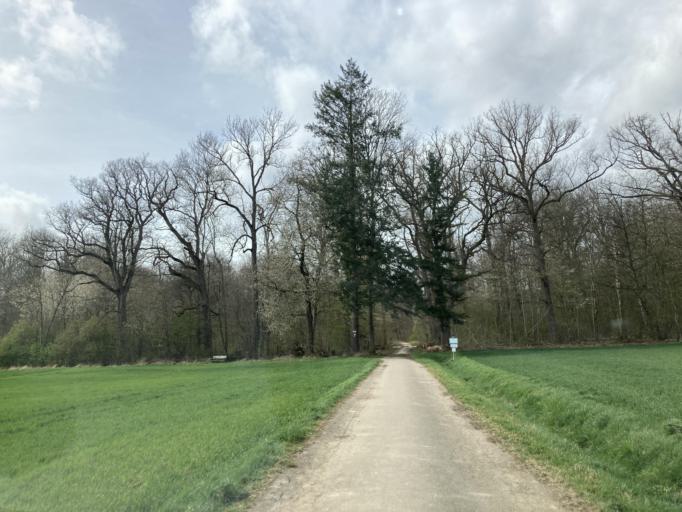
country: DE
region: Baden-Wuerttemberg
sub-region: Tuebingen Region
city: Gomaringen
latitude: 48.4879
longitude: 9.0881
